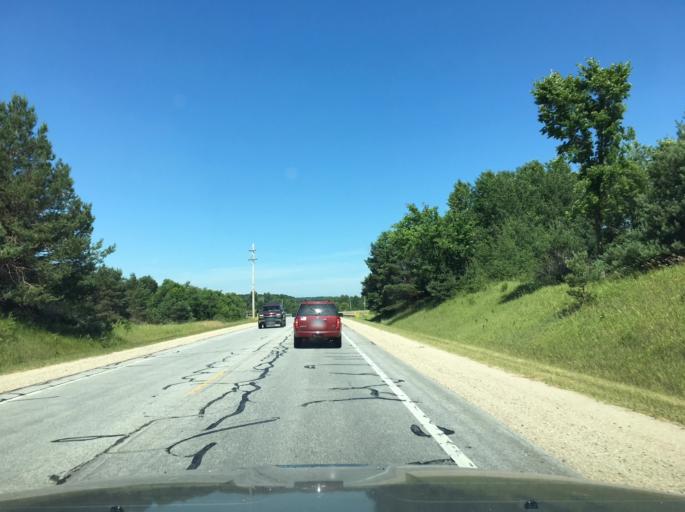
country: US
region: Michigan
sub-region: Osceola County
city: Reed City
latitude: 43.8779
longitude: -85.4996
